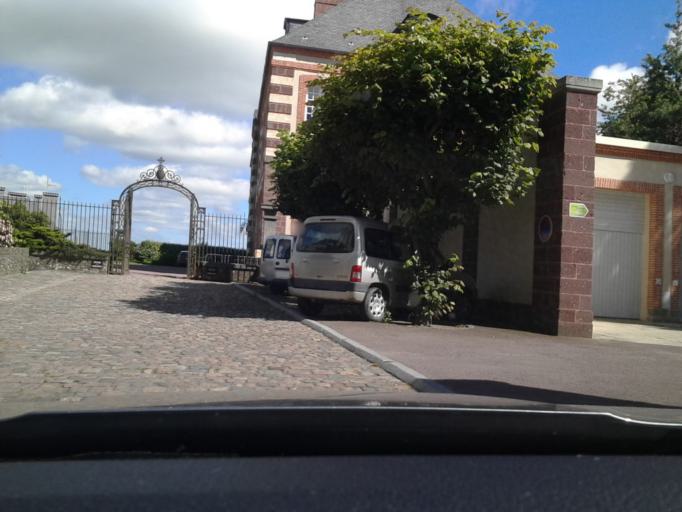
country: FR
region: Lower Normandy
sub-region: Departement de la Manche
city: Coutances
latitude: 49.0473
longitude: -1.4439
